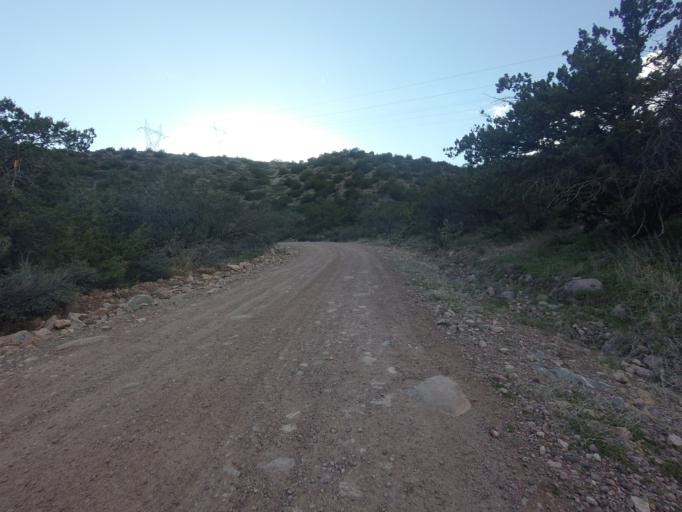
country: US
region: Arizona
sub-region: Gila County
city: Pine
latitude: 34.3764
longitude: -111.6638
